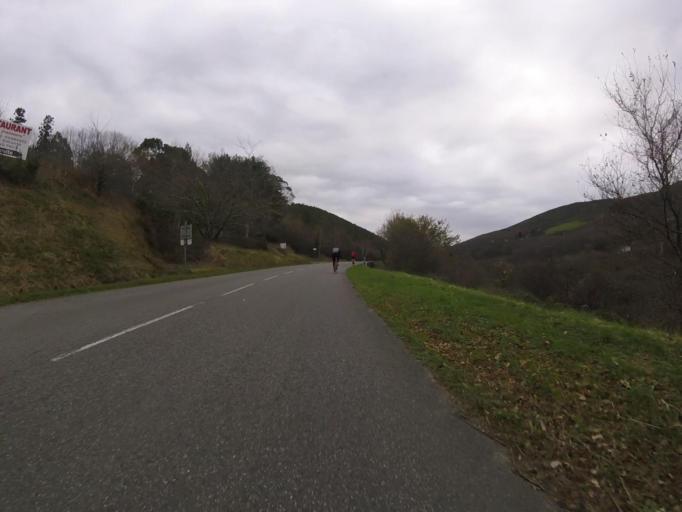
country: FR
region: Aquitaine
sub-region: Departement des Pyrenees-Atlantiques
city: Ascain
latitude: 43.3311
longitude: -1.6028
